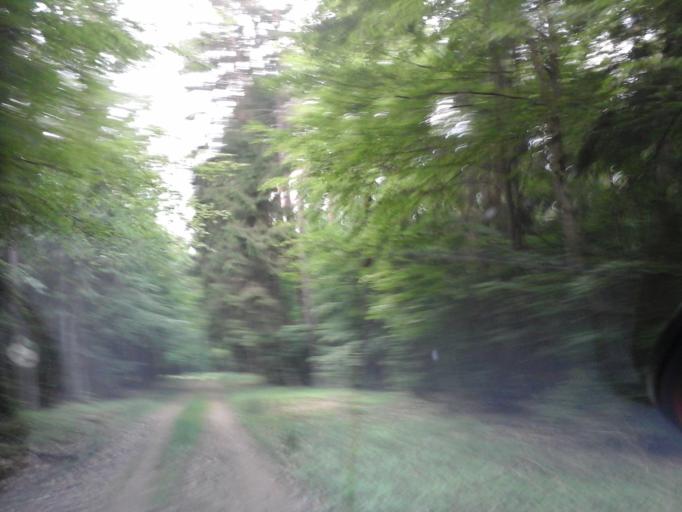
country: PL
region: West Pomeranian Voivodeship
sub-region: Powiat choszczenski
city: Drawno
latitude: 53.1198
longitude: 15.8875
